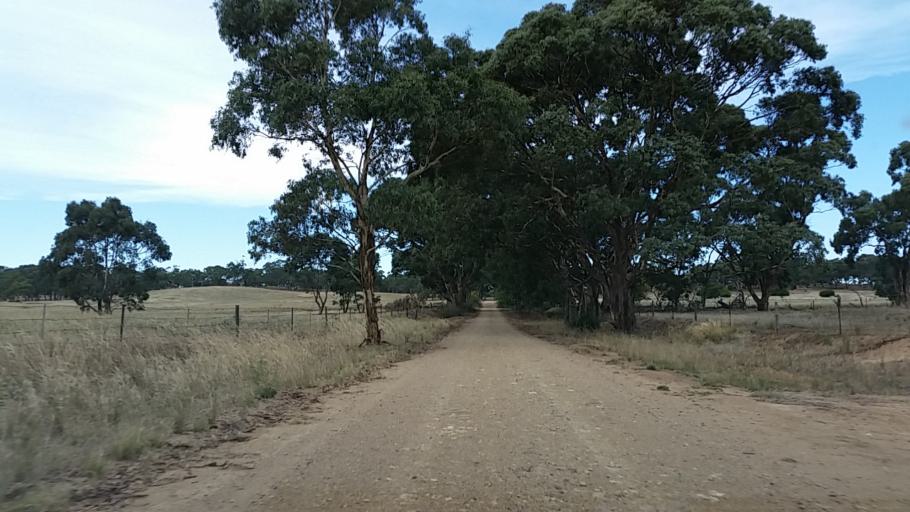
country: AU
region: South Australia
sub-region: Barossa
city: Angaston
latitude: -34.4509
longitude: 139.0516
